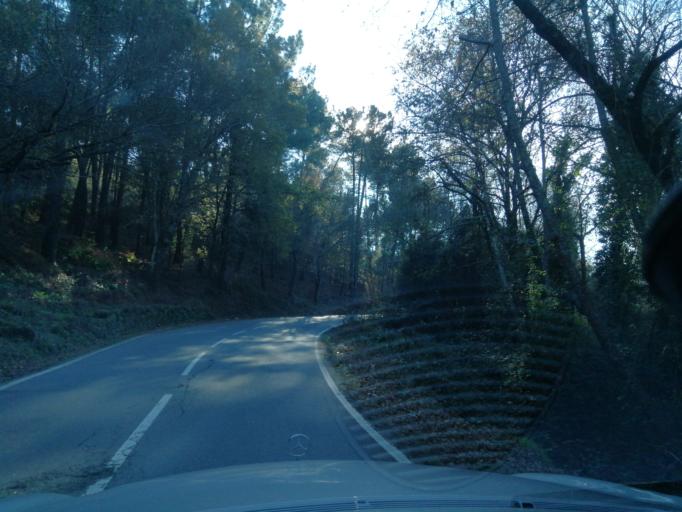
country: PT
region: Braga
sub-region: Braga
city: Adaufe
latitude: 41.5749
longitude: -8.3877
